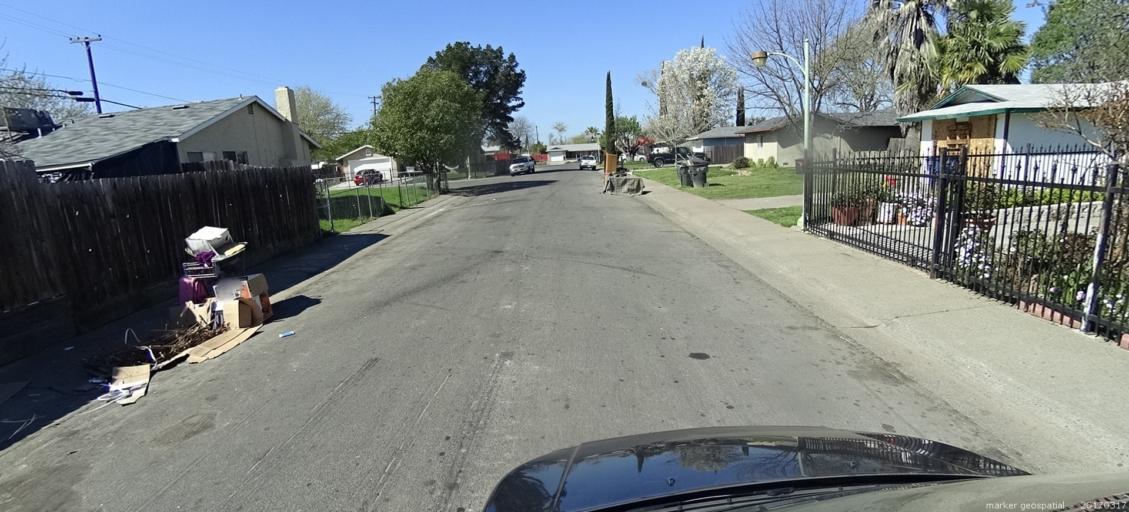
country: US
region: California
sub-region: Sacramento County
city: Parkway
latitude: 38.4856
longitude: -121.4864
